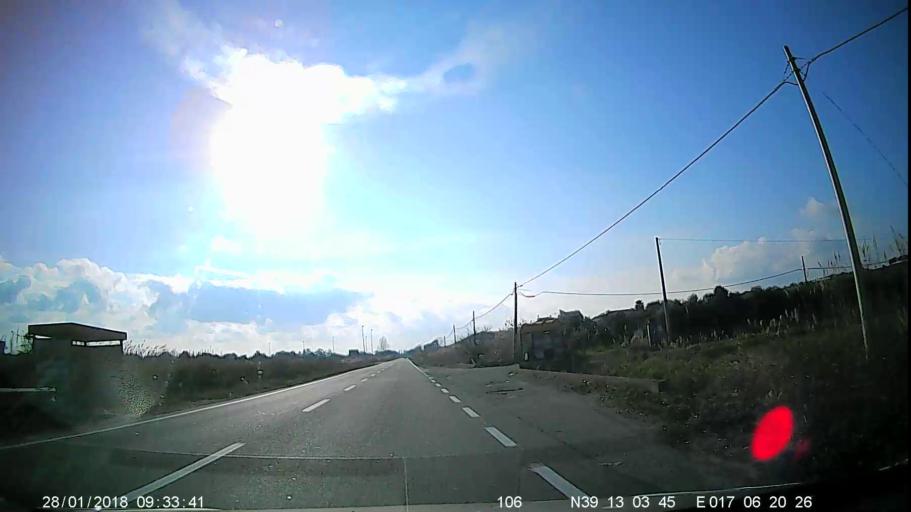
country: IT
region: Calabria
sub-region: Provincia di Crotone
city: Tronca
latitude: 39.2172
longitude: 17.1059
